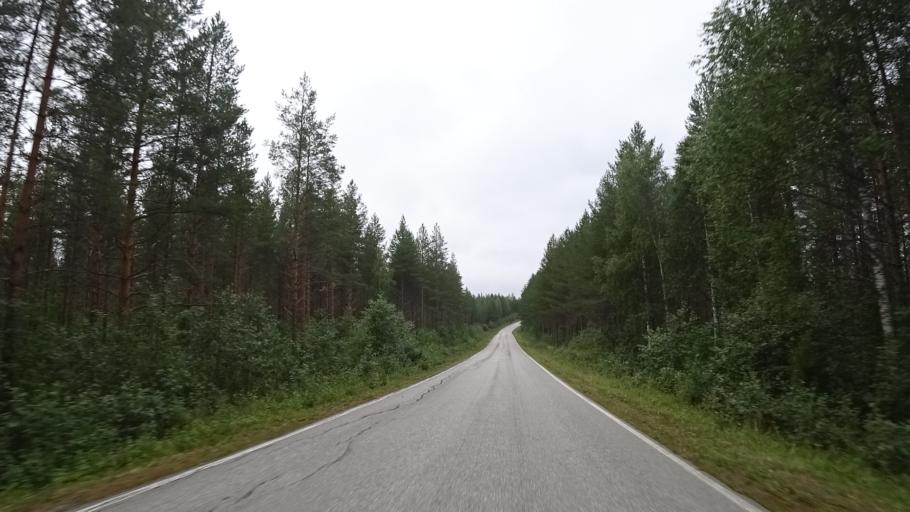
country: FI
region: North Karelia
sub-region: Pielisen Karjala
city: Lieksa
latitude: 63.3660
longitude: 30.2892
